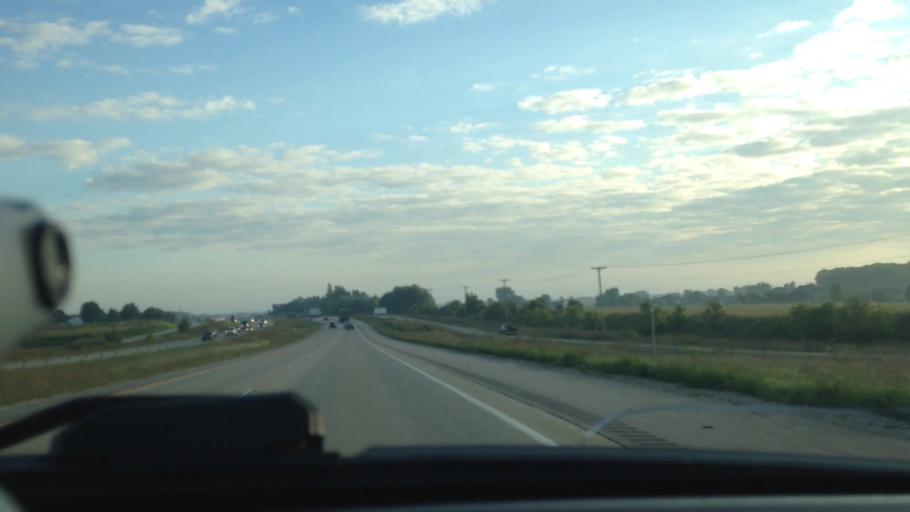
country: US
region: Wisconsin
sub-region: Brown County
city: Wrightstown
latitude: 44.3288
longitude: -88.2097
